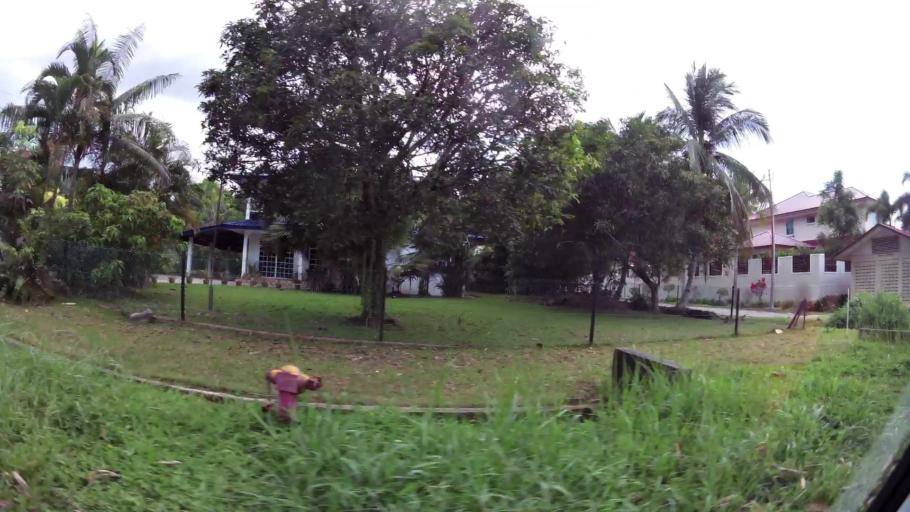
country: BN
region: Brunei and Muara
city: Bandar Seri Begawan
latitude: 4.9533
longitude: 114.9730
